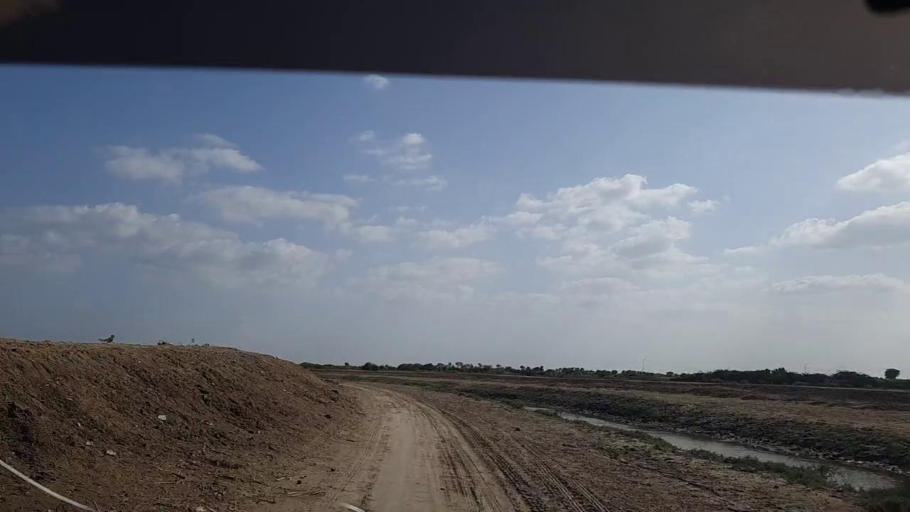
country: PK
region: Sindh
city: Kadhan
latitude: 24.4533
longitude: 68.8580
